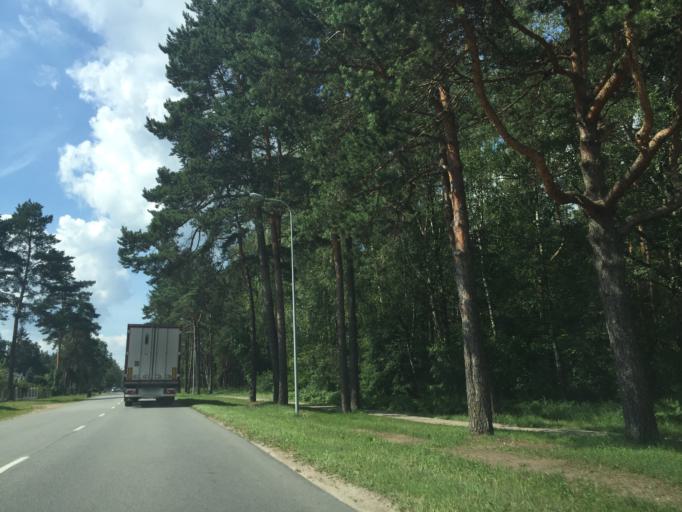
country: LV
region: Kekava
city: Balozi
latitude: 56.8736
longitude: 24.1153
